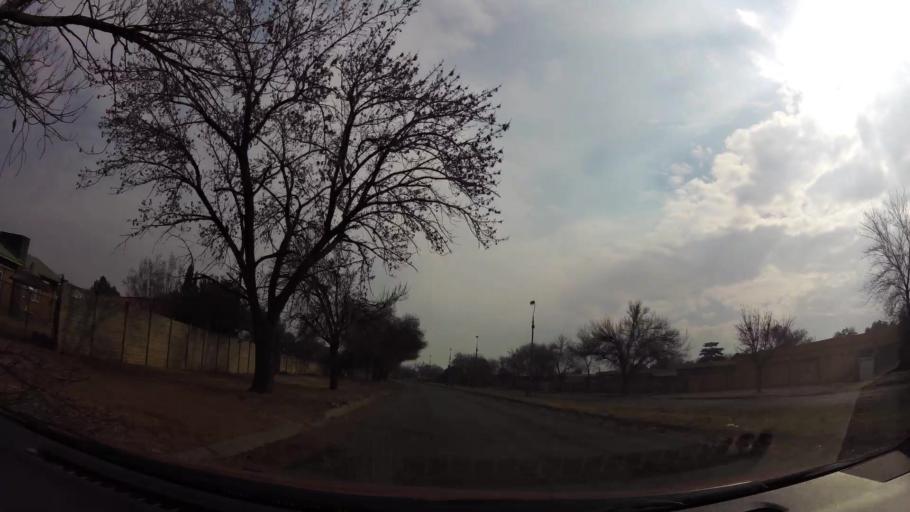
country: ZA
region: Gauteng
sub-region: Sedibeng District Municipality
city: Vanderbijlpark
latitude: -26.6891
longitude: 27.8456
